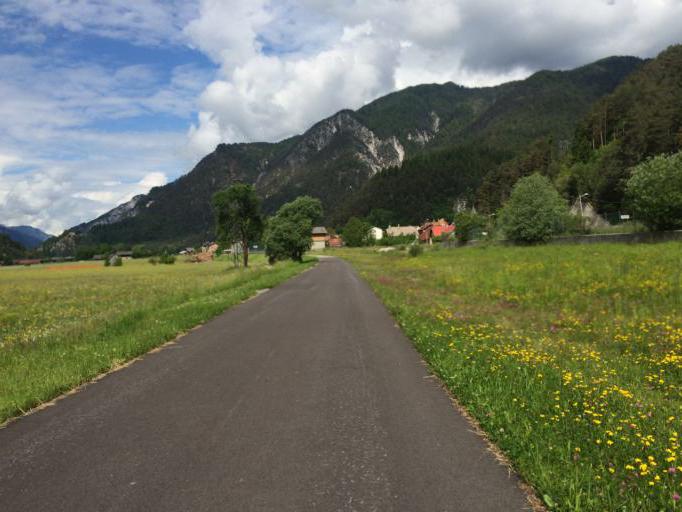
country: IT
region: Friuli Venezia Giulia
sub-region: Provincia di Udine
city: Malborghetto
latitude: 46.5091
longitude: 13.4794
